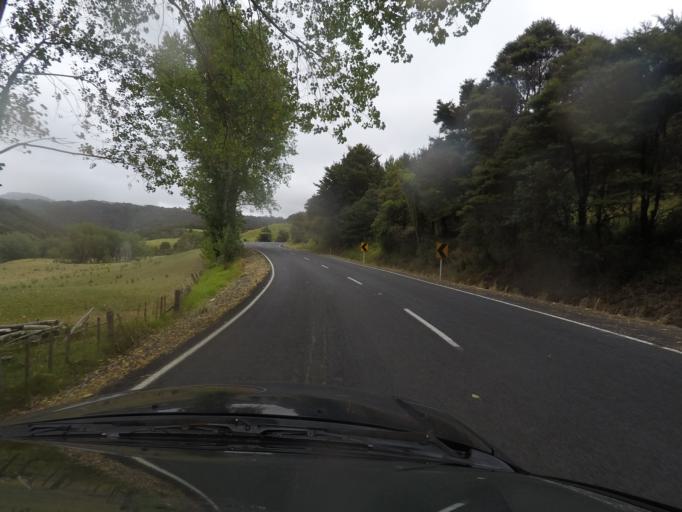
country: NZ
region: Auckland
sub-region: Auckland
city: Warkworth
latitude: -36.2713
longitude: 174.6986
